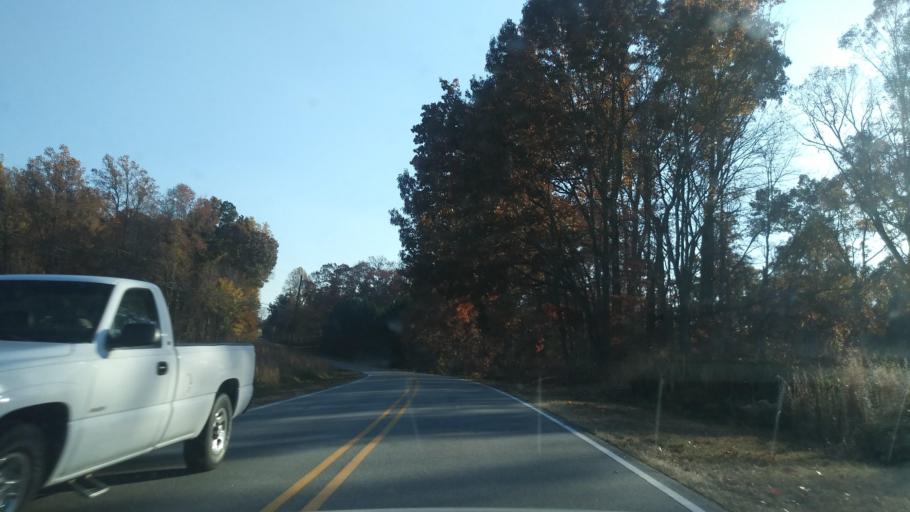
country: US
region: North Carolina
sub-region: Guilford County
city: McLeansville
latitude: 36.2235
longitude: -79.7200
